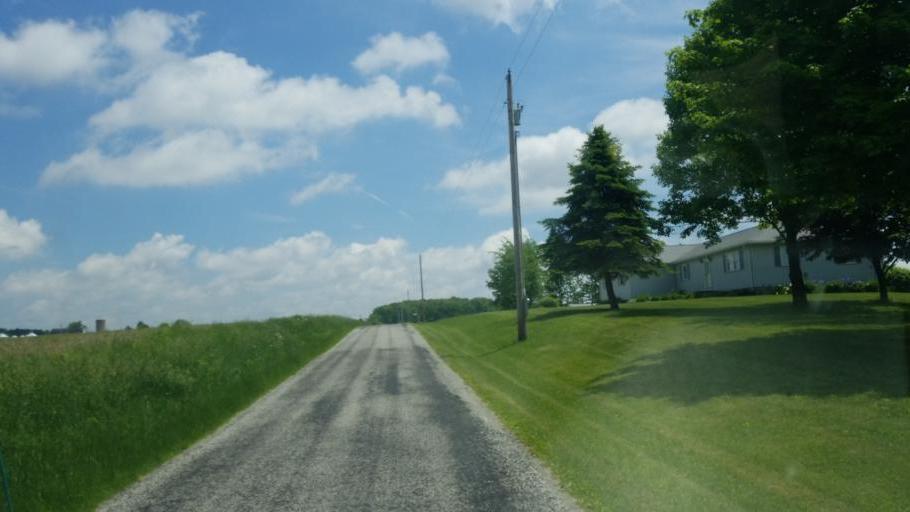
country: US
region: Ohio
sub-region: Ashland County
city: Ashland
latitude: 40.8424
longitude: -82.1979
